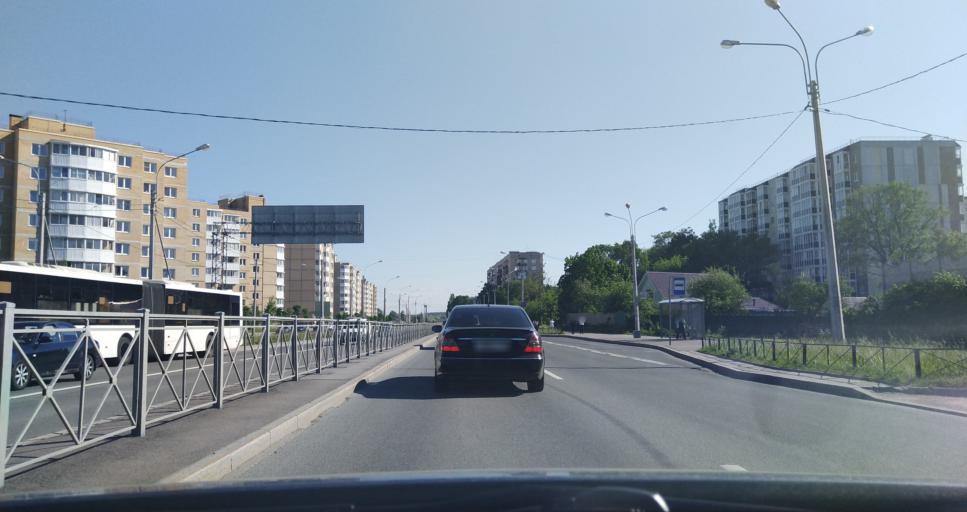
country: RU
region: St.-Petersburg
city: Krasnoye Selo
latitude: 59.7235
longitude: 30.0799
